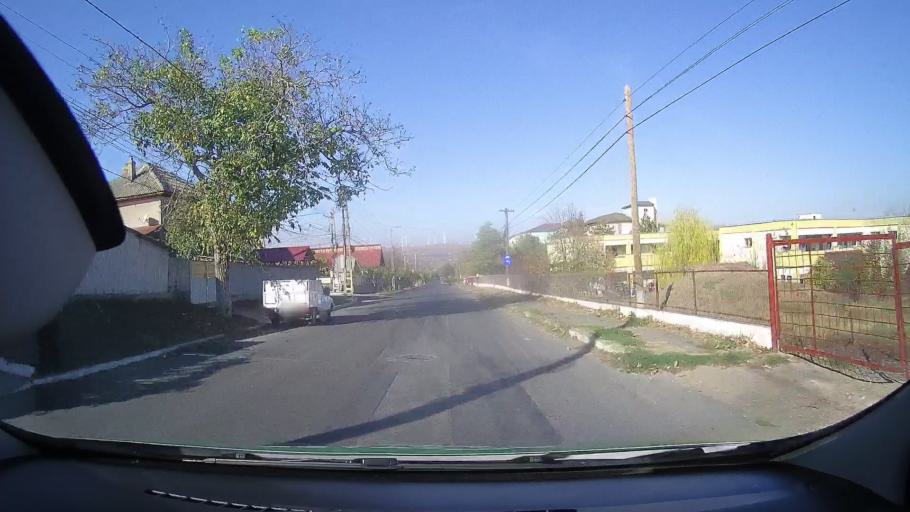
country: RO
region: Tulcea
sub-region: Oras Babadag
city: Babadag
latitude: 44.8870
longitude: 28.7337
